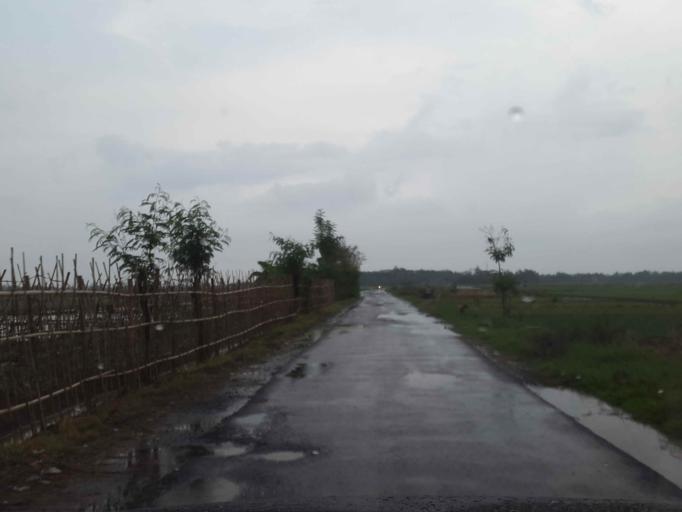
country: ID
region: Central Java
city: Ketanggungan
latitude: -6.9799
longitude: 108.9024
